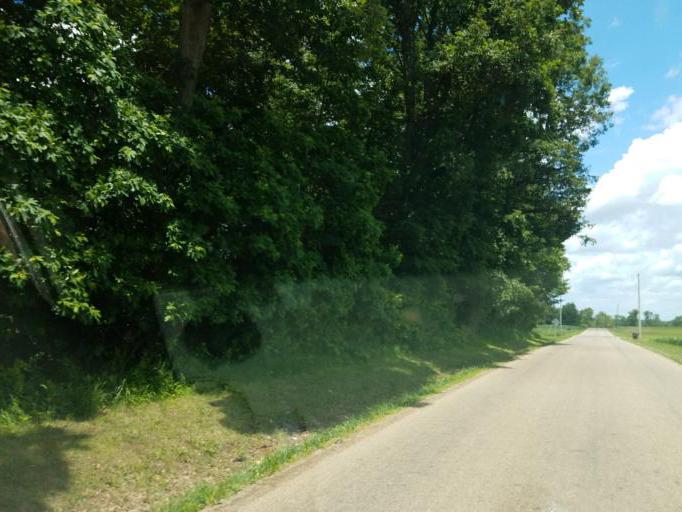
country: US
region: Ohio
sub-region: Knox County
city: Oak Hill
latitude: 40.3643
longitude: -82.3105
